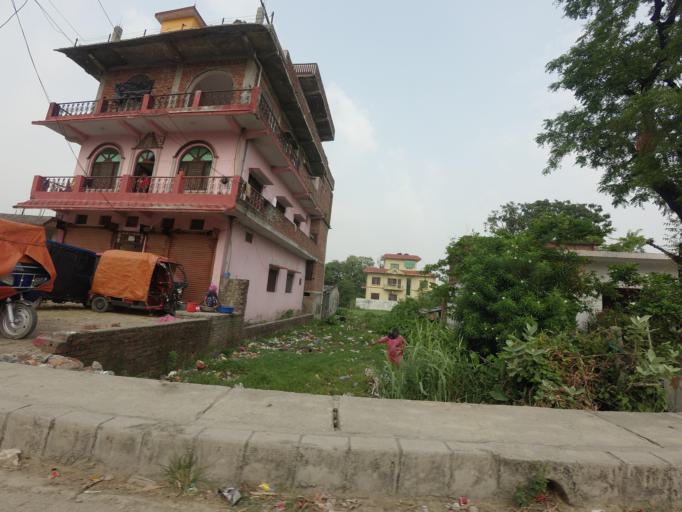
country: NP
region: Western Region
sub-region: Lumbini Zone
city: Bhairahawa
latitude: 27.4961
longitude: 83.4494
